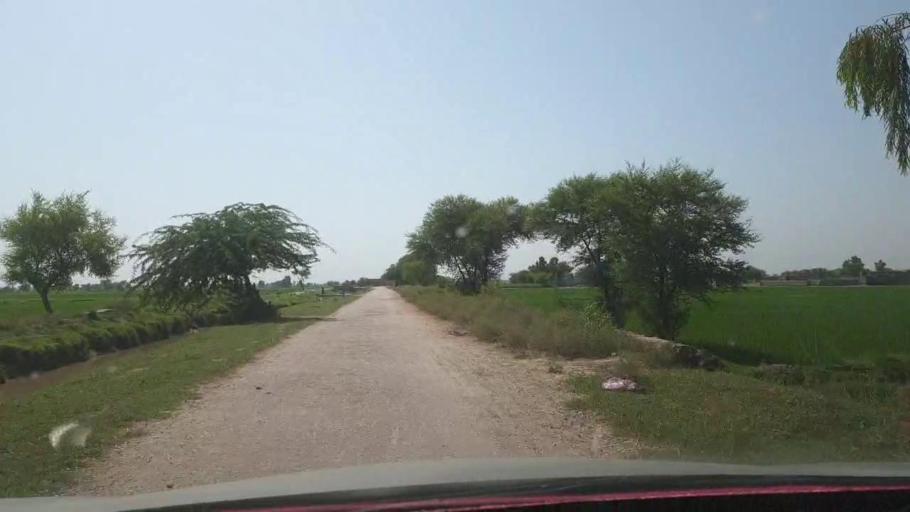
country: PK
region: Sindh
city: Warah
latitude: 27.4063
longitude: 67.8075
